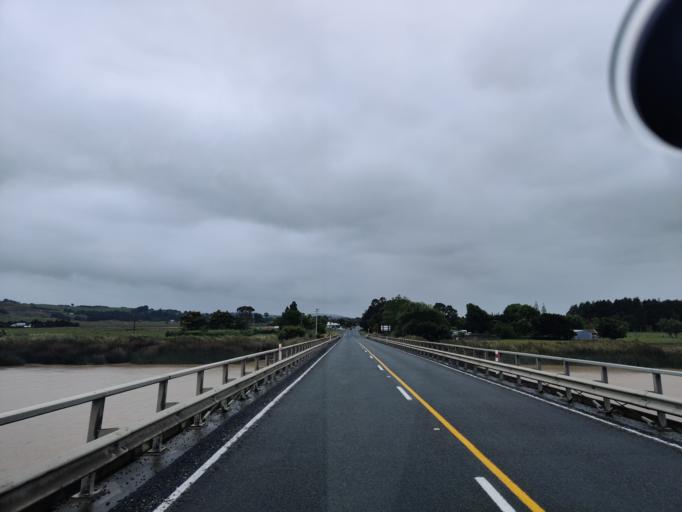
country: NZ
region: Northland
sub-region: Kaipara District
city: Dargaville
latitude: -35.9402
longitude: 173.8847
